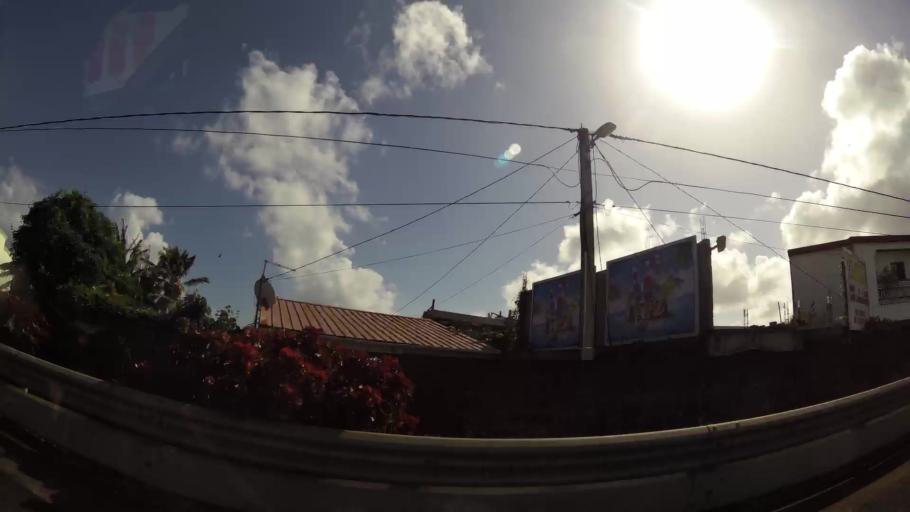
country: MQ
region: Martinique
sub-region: Martinique
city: Sainte-Marie
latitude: 14.7807
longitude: -60.9915
